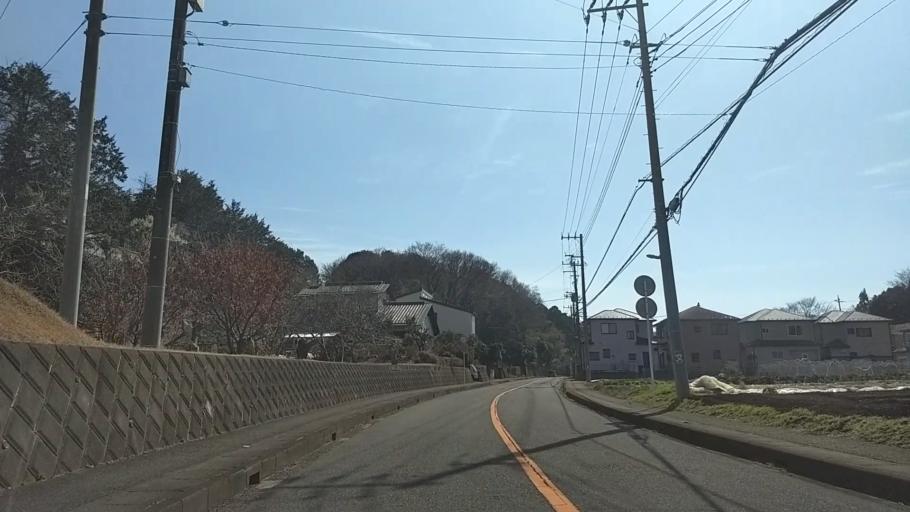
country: JP
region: Kanagawa
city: Fujisawa
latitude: 35.3764
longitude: 139.4285
